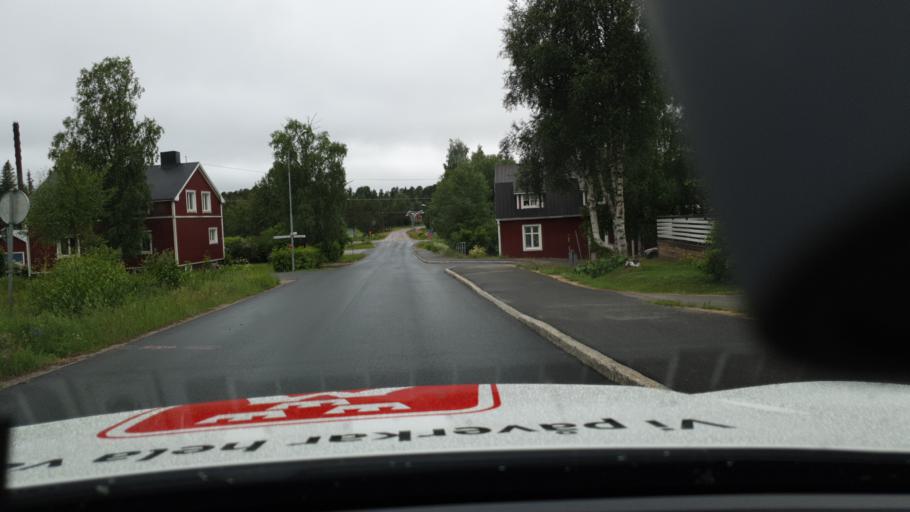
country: SE
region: Norrbotten
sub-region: Overtornea Kommun
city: OEvertornea
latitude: 66.3888
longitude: 23.6429
